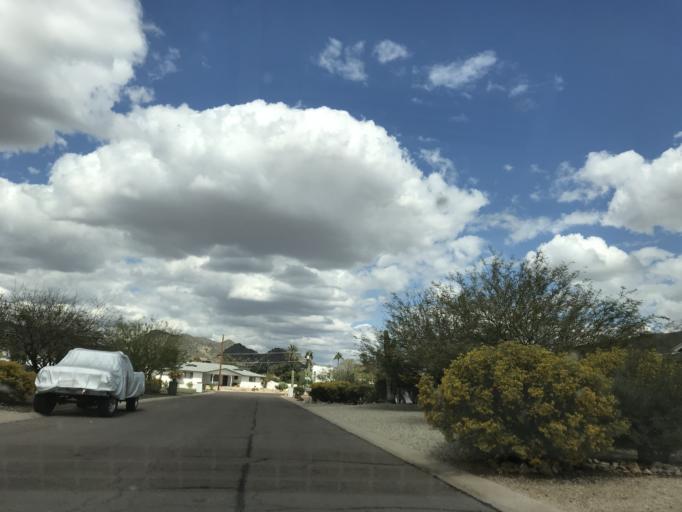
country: US
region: Arizona
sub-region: Maricopa County
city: Paradise Valley
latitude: 33.5150
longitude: -111.9903
